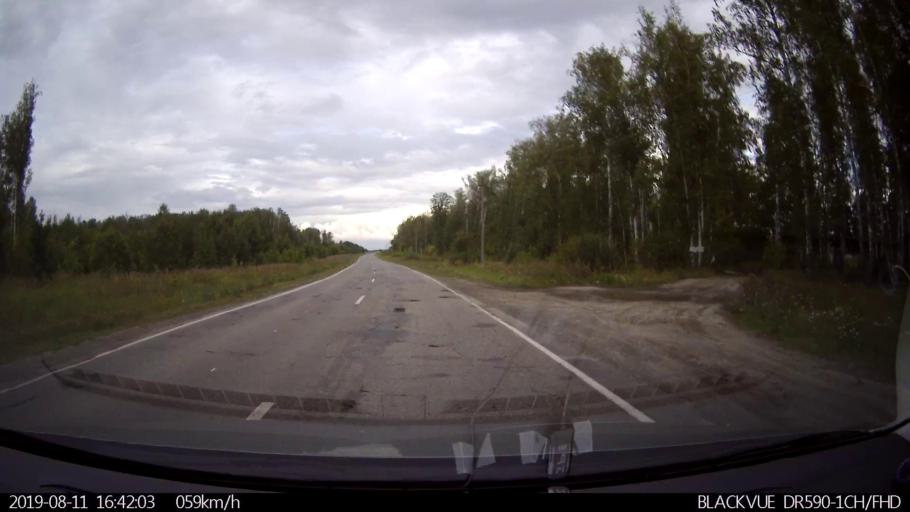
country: RU
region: Ulyanovsk
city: Mayna
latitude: 54.1575
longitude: 47.6590
